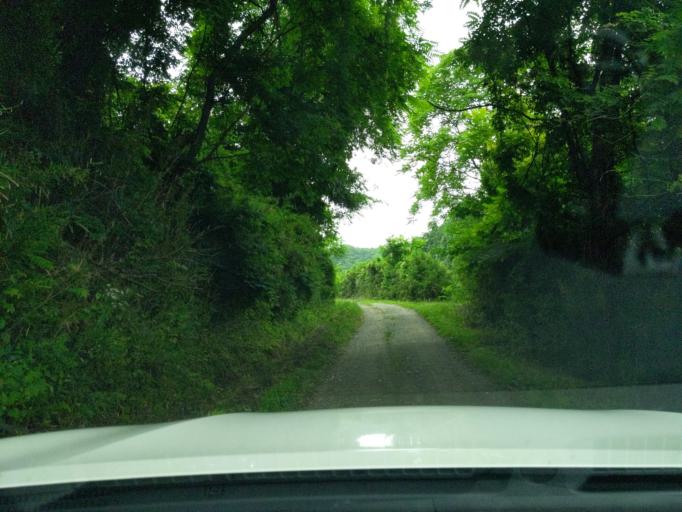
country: JP
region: Fukushima
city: Koriyama
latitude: 37.4011
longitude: 140.4332
